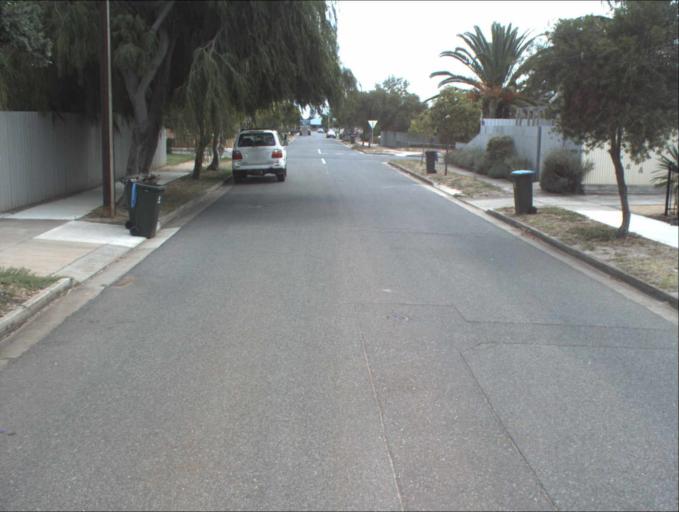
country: AU
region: South Australia
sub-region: Port Adelaide Enfield
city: Birkenhead
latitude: -34.8072
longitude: 138.4954
